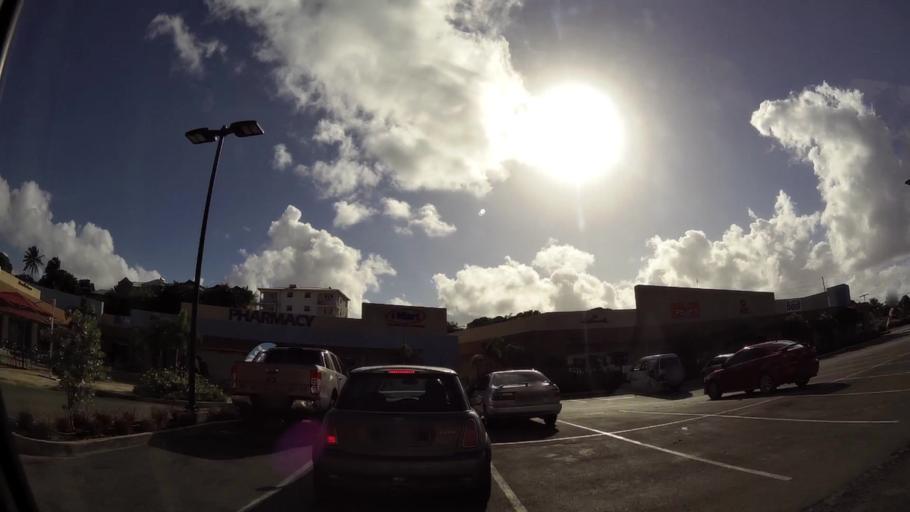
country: BB
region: Saint James
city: Holetown
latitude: 13.1549
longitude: -59.6114
